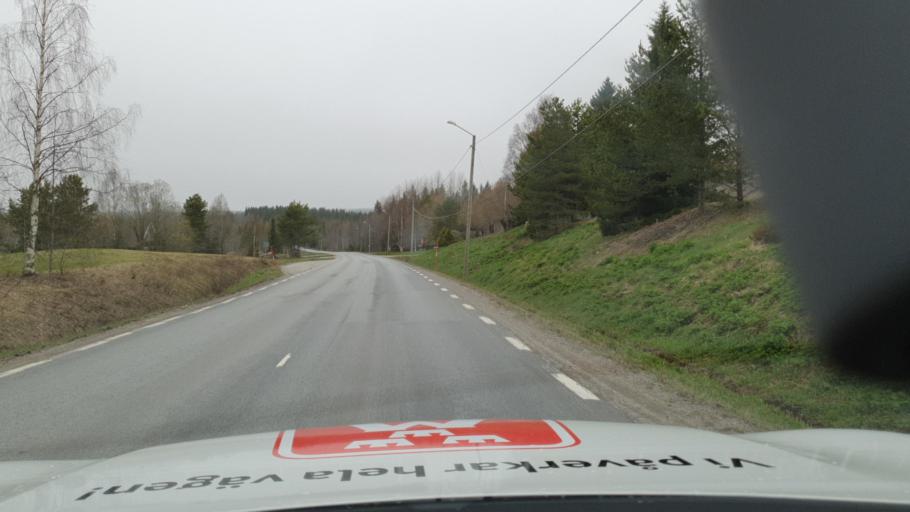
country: SE
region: Vaesterbotten
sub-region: Vannas Kommun
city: Vaennaes
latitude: 63.7756
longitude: 19.6642
